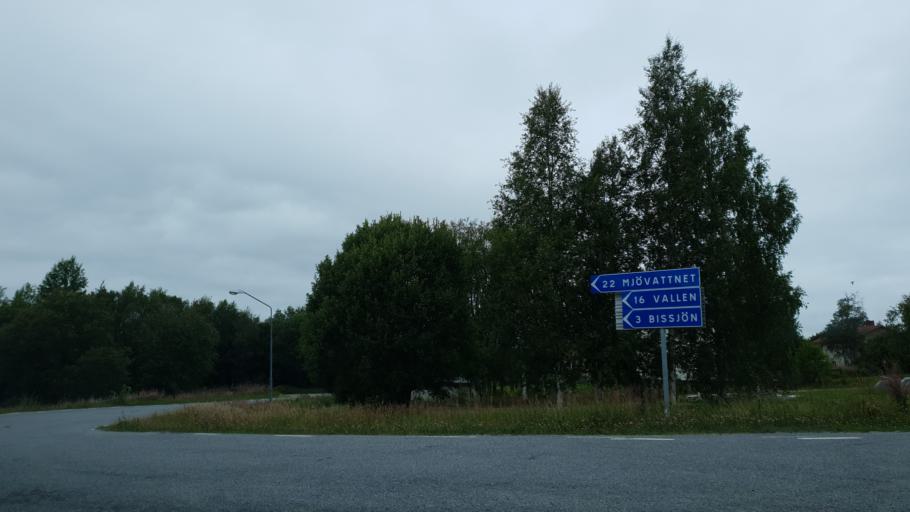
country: SE
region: Vaesterbotten
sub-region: Skelleftea Kommun
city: Burea
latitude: 64.4022
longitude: 21.2900
